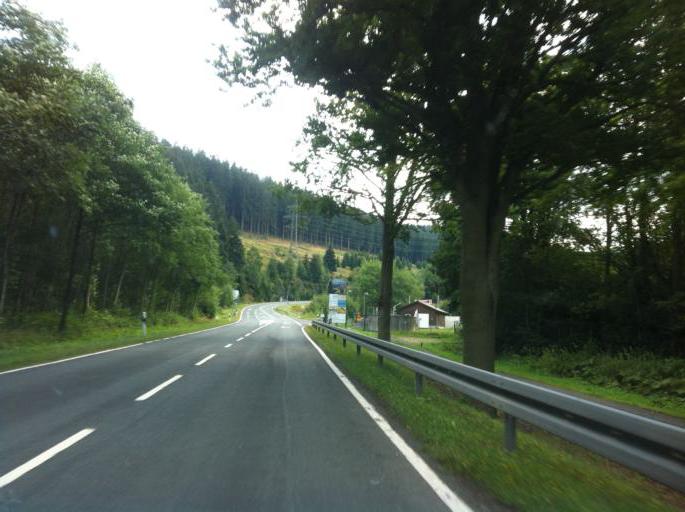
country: DE
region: Thuringia
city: Goldisthal
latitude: 50.5284
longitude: 11.0141
